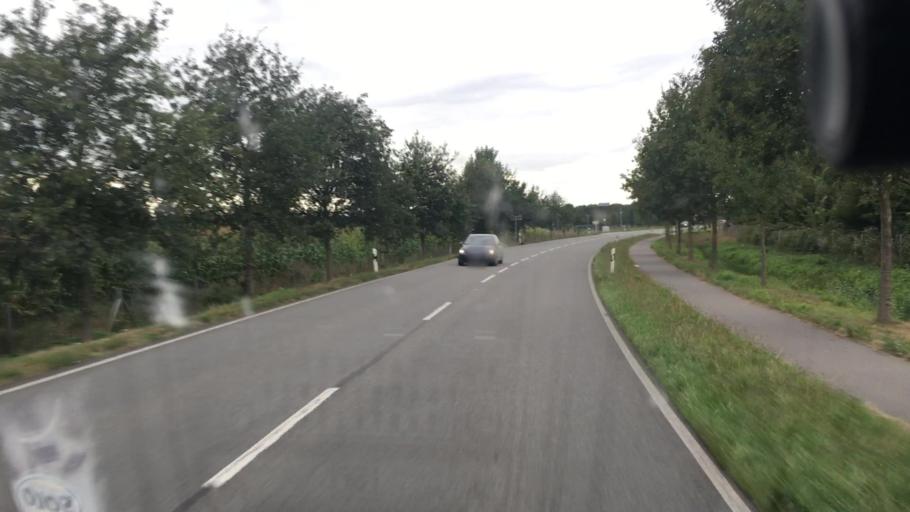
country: DE
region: Lower Saxony
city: Lohne
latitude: 52.6501
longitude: 8.2047
